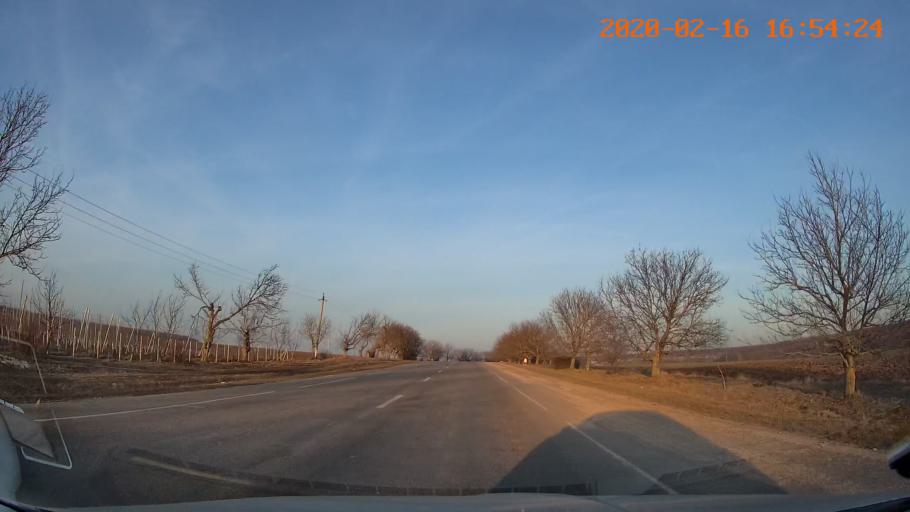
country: MD
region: Briceni
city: Briceni
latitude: 48.3205
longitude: 27.0060
